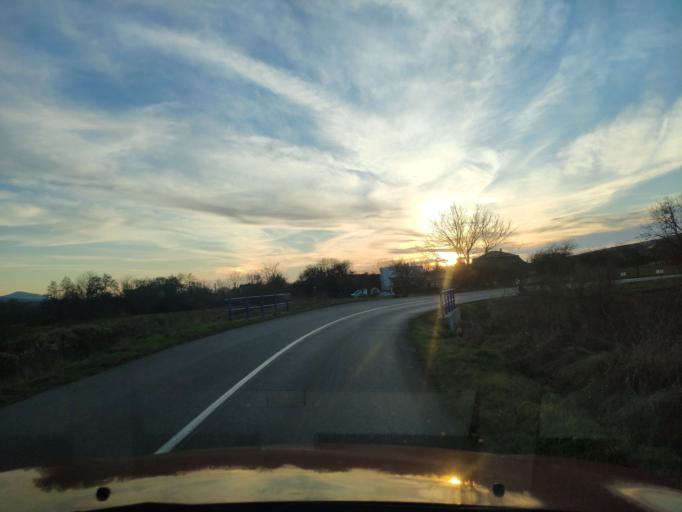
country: SK
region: Kosicky
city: Kosice
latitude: 48.6676
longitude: 21.4023
